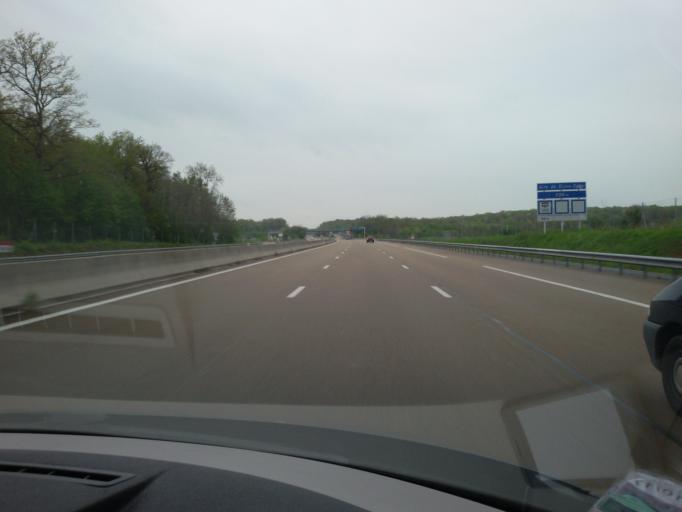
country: FR
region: Bourgogne
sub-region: Departement de la Cote-d'Or
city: Saint-Julien
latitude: 47.4175
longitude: 5.1753
